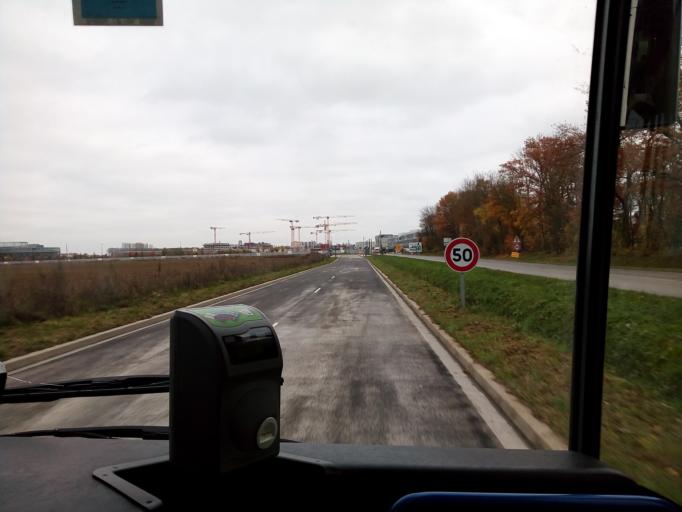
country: FR
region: Ile-de-France
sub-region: Departement de l'Essonne
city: Orsay
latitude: 48.7139
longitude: 2.1886
